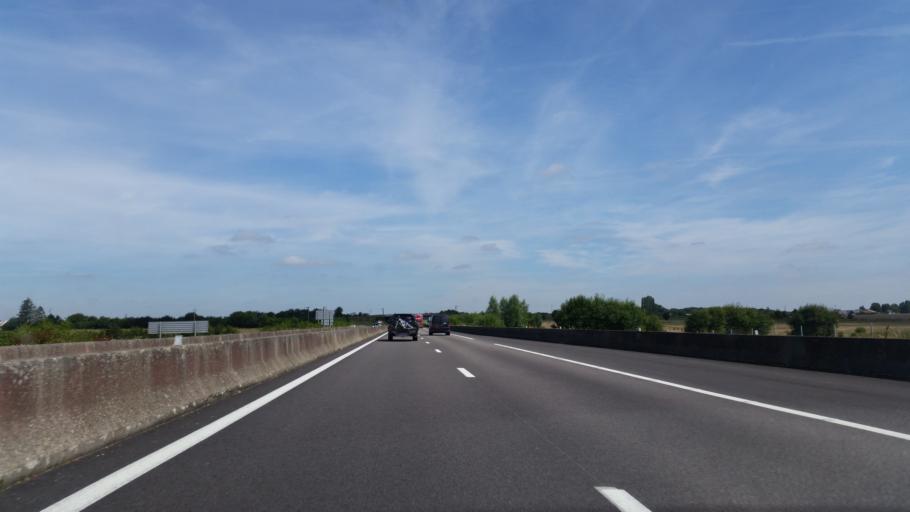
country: FR
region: Haute-Normandie
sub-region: Departement de la Seine-Maritime
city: Aumale
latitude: 49.7669
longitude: 1.7100
